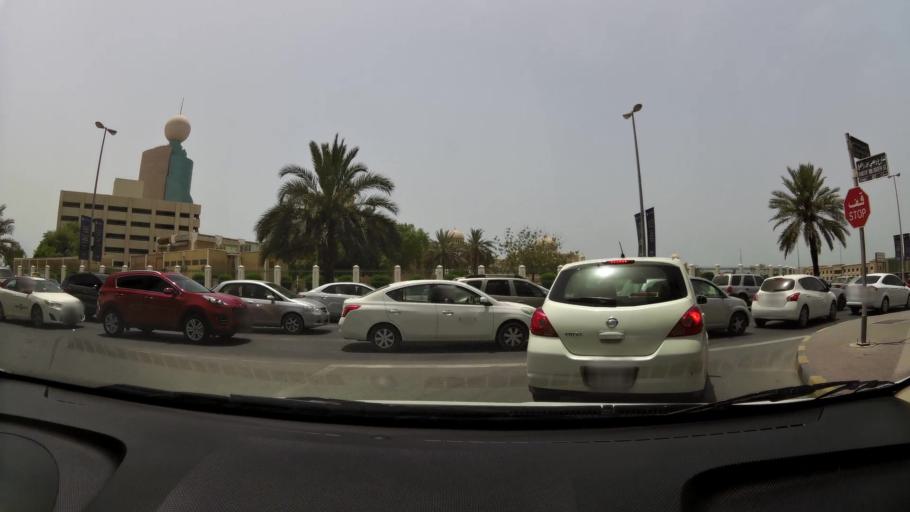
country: AE
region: Ash Shariqah
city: Sharjah
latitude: 25.3550
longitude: 55.4032
